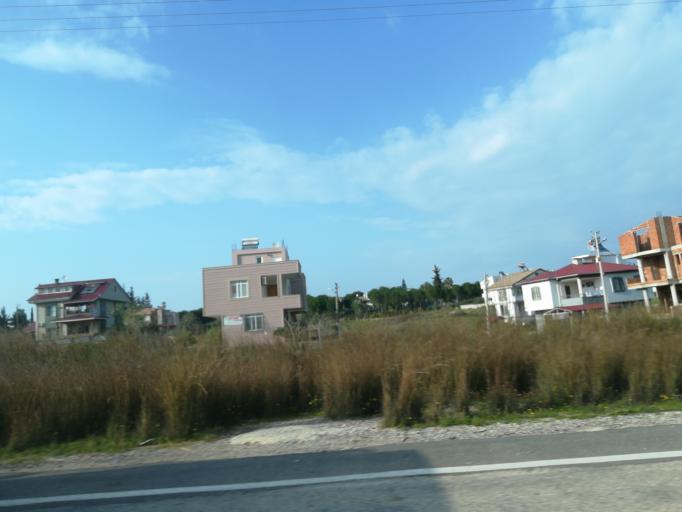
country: TR
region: Adana
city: Adana
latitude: 37.0779
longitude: 35.3906
